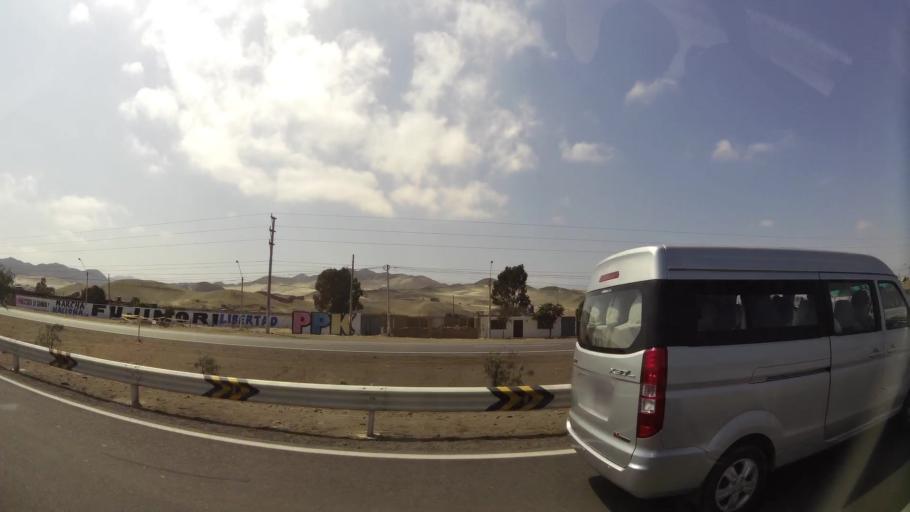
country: PE
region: Lima
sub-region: Provincia de Canete
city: Asia
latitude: -12.7658
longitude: -76.5965
